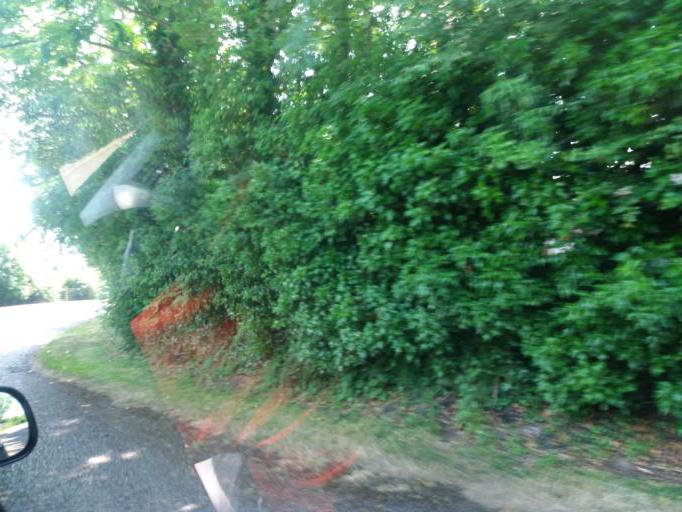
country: IE
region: Leinster
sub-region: An Mhi
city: Slane
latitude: 53.7159
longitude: -6.5376
